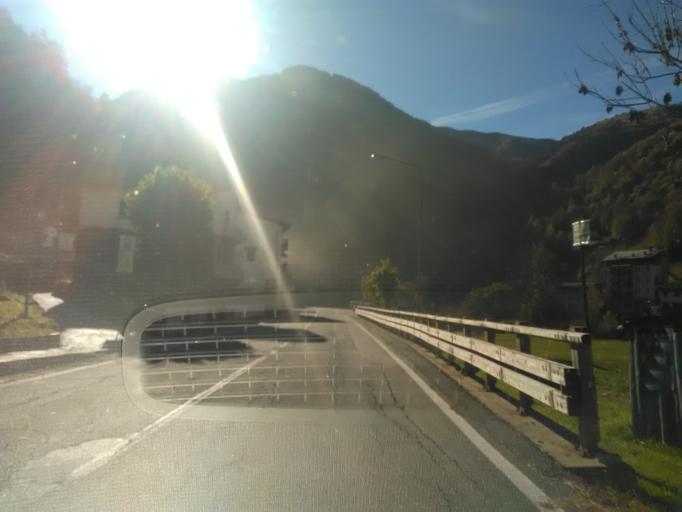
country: IT
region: Piedmont
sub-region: Provincia di Vercelli
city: Piode
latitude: 45.7729
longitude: 8.0504
